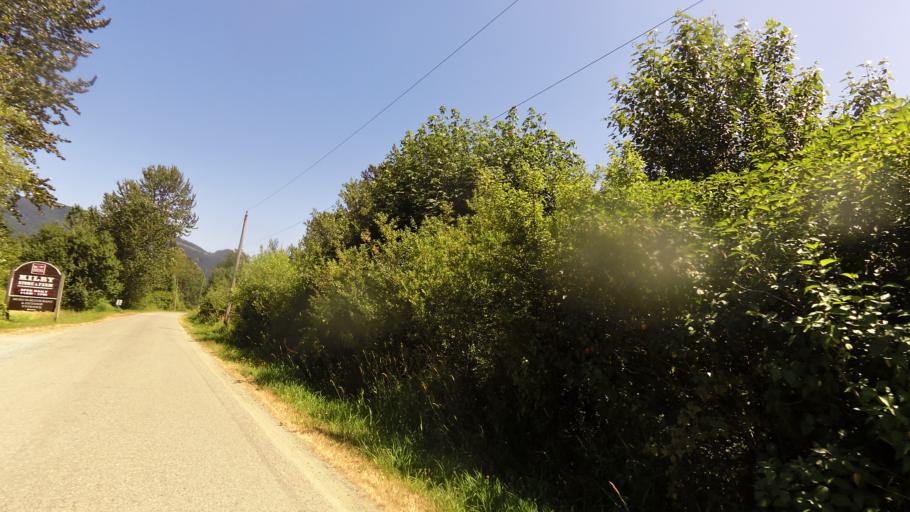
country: CA
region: British Columbia
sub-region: Fraser Valley Regional District
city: Chilliwack
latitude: 49.2360
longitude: -121.9555
